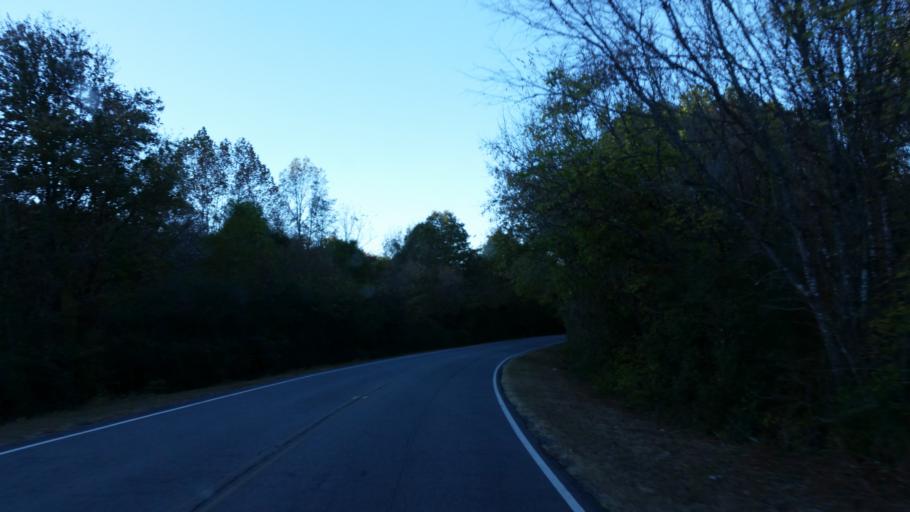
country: US
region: Georgia
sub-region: Bartow County
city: Adairsville
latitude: 34.3631
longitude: -84.9434
